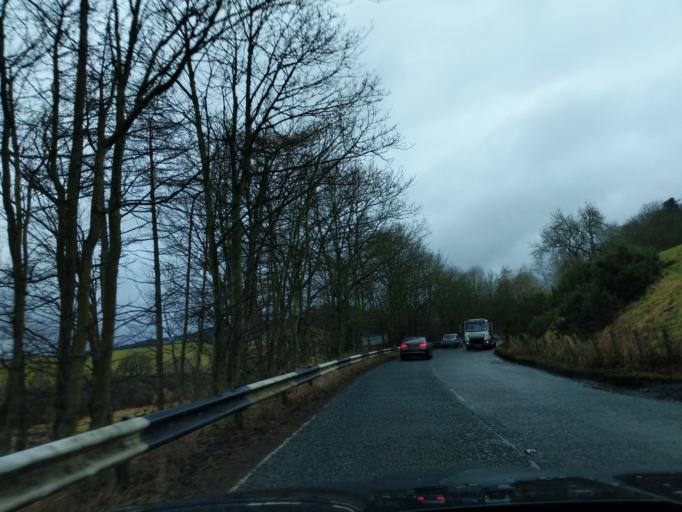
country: GB
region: Scotland
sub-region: The Scottish Borders
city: Galashiels
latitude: 55.6450
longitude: -2.8543
